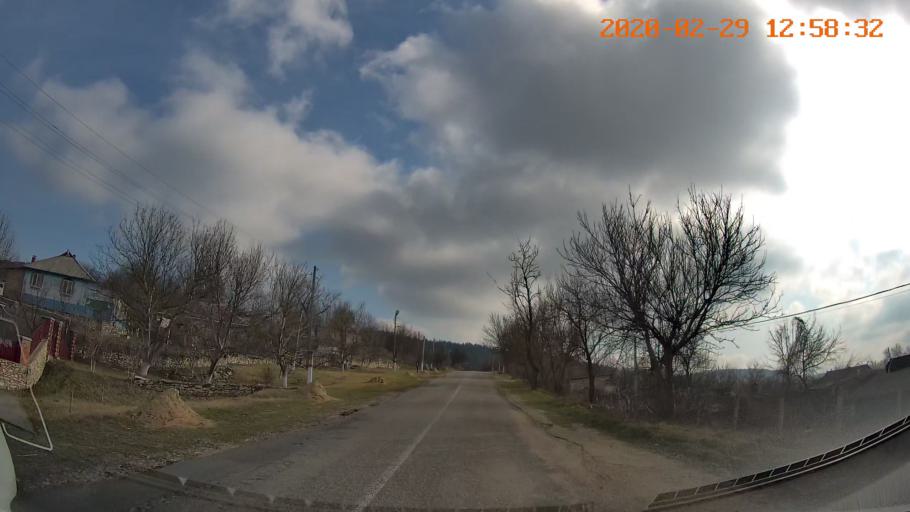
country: MD
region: Telenesti
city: Camenca
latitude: 48.0697
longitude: 28.7217
